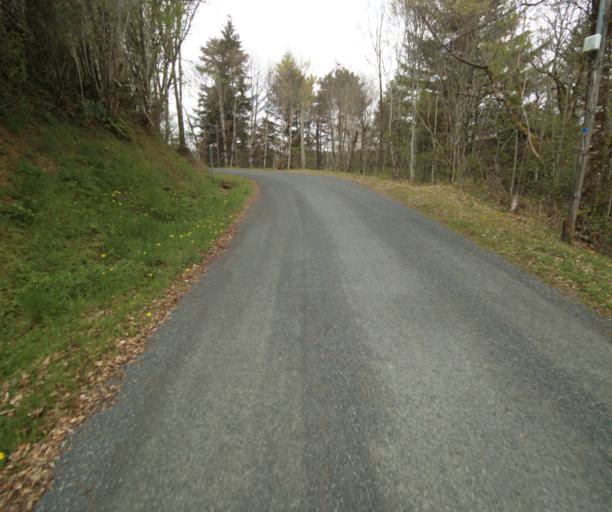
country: FR
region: Limousin
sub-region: Departement de la Correze
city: Sainte-Fortunade
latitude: 45.1918
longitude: 1.8632
